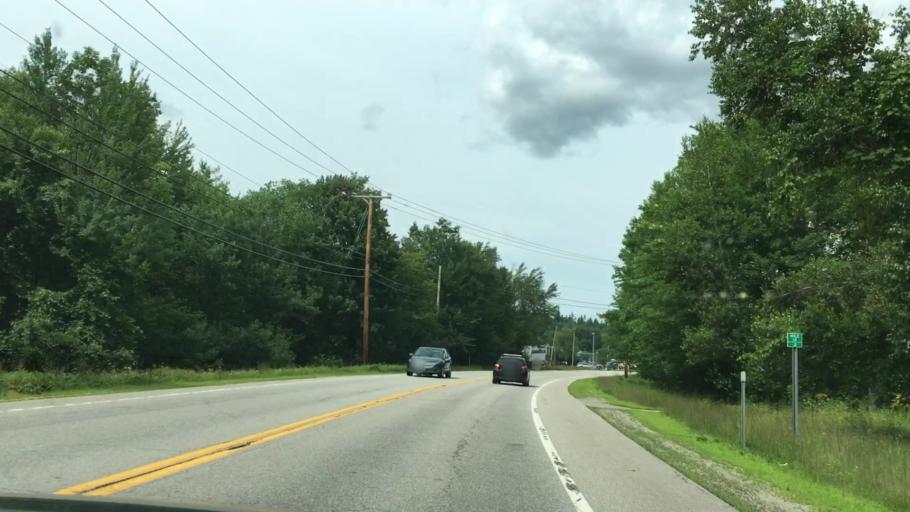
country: US
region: New Hampshire
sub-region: Hillsborough County
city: Peterborough
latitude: 42.8518
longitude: -71.9652
